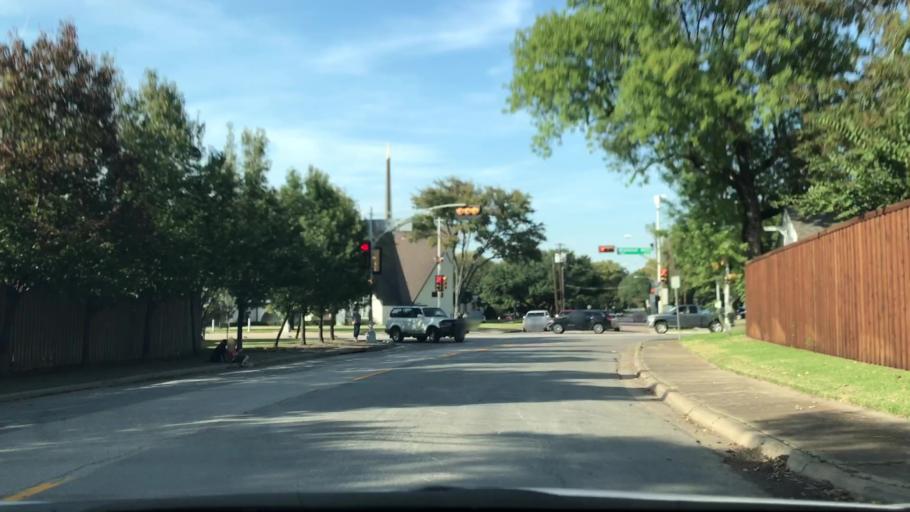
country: US
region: Texas
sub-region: Dallas County
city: University Park
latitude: 32.8795
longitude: -96.7964
